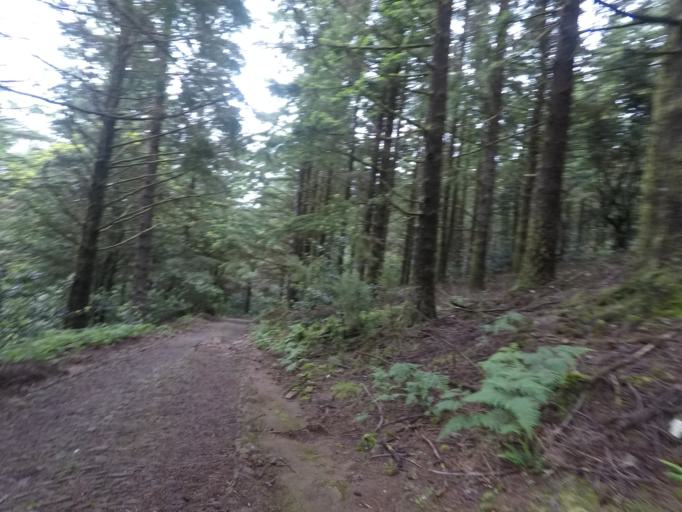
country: PT
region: Madeira
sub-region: Funchal
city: Nossa Senhora do Monte
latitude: 32.7175
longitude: -16.8861
